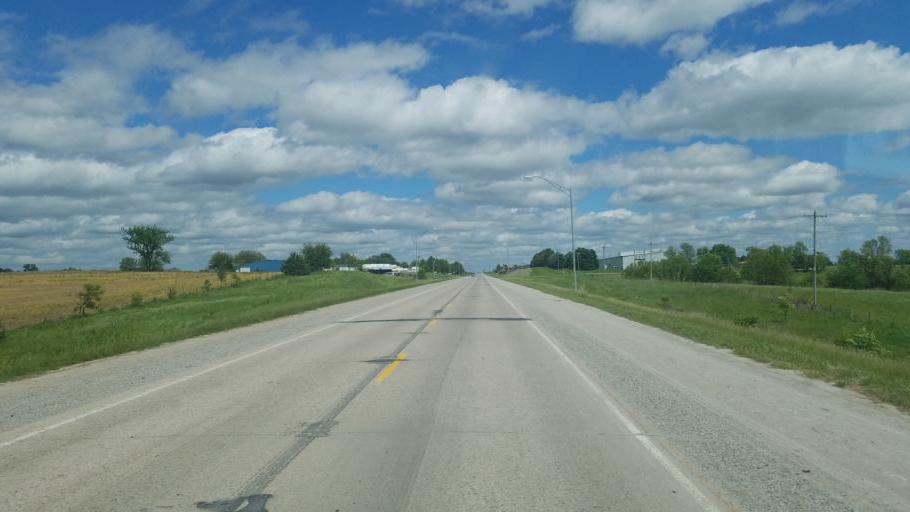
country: US
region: Iowa
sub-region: Decatur County
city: Lamoni
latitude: 40.6236
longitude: -93.9086
